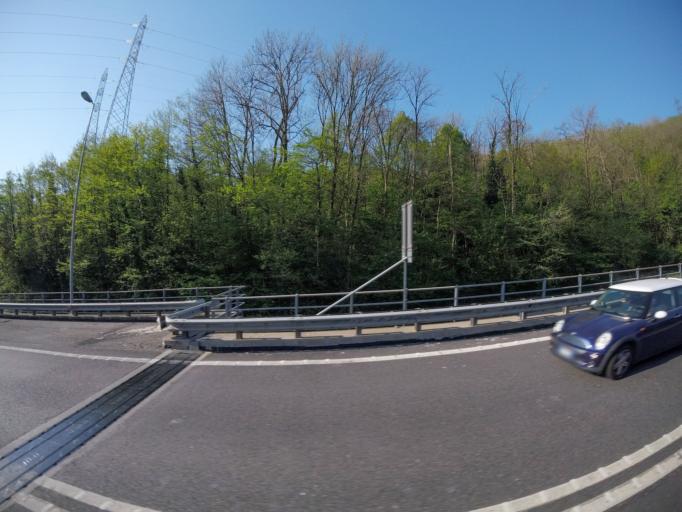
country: IT
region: Lombardy
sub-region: Provincia di Como
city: Maslianico
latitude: 45.8380
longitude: 9.0514
